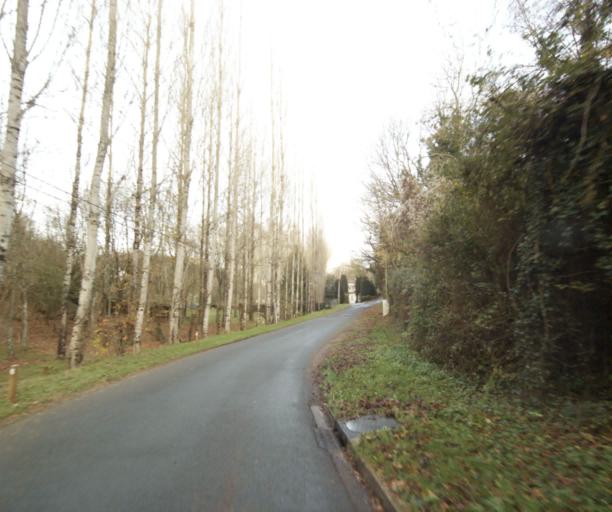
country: FR
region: Poitou-Charentes
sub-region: Departement de la Charente-Maritime
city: Fontcouverte
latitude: 45.7730
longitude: -0.5923
